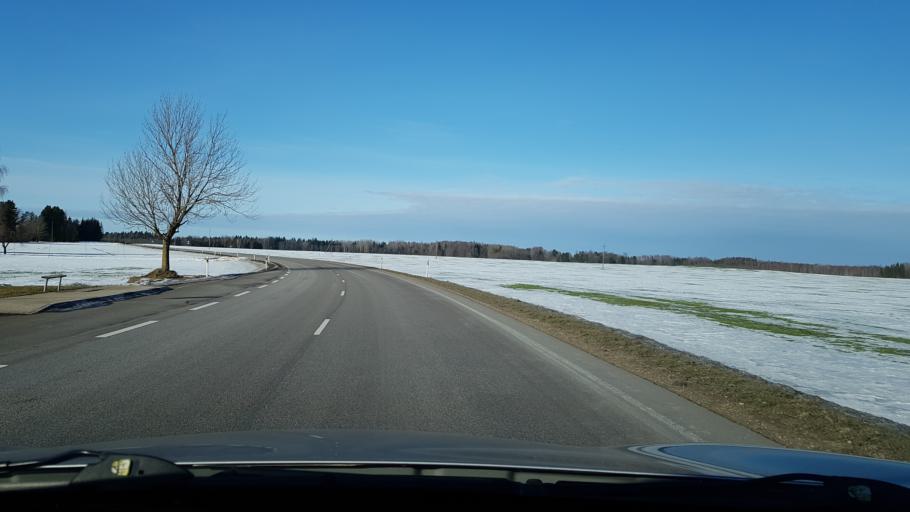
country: EE
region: Jogevamaa
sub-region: Poltsamaa linn
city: Poltsamaa
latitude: 58.6370
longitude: 25.7730
